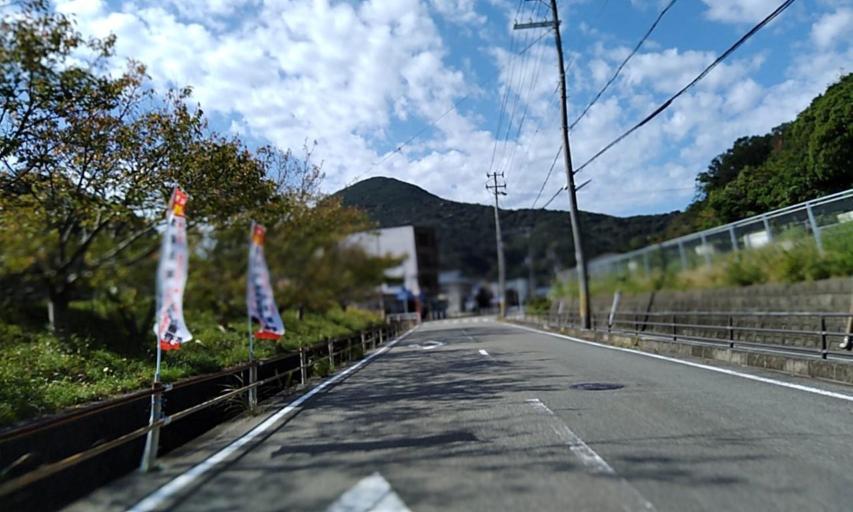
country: JP
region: Wakayama
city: Gobo
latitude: 33.9687
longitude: 135.1052
